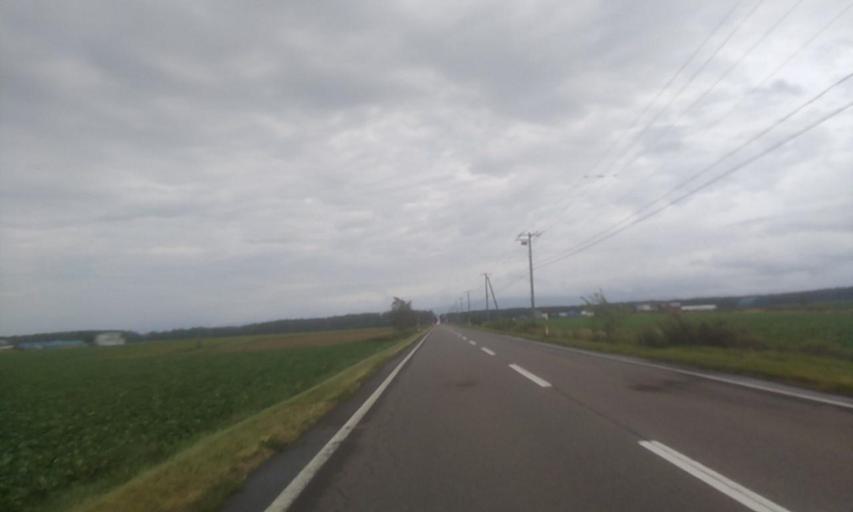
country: JP
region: Hokkaido
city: Abashiri
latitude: 43.8938
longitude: 144.5161
